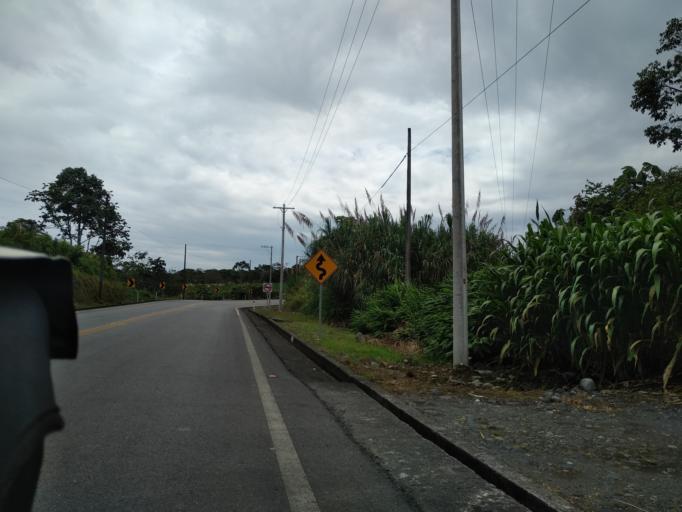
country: EC
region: Pastaza
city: Puyo
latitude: -1.3577
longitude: -77.9353
